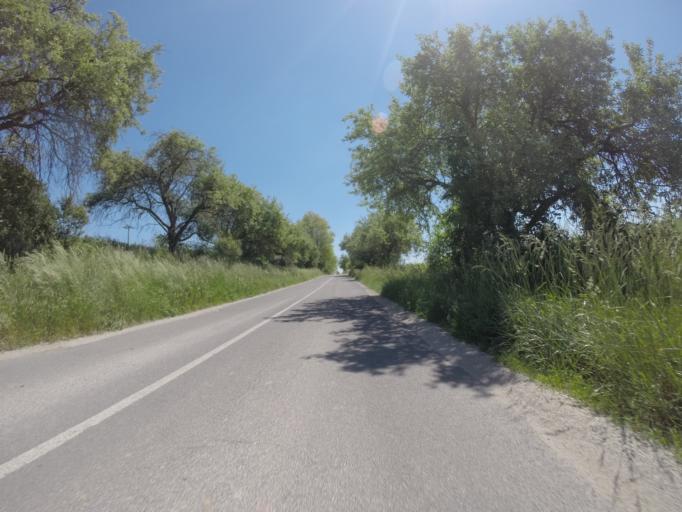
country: SK
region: Trnavsky
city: Hlohovec
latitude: 48.4806
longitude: 17.8880
